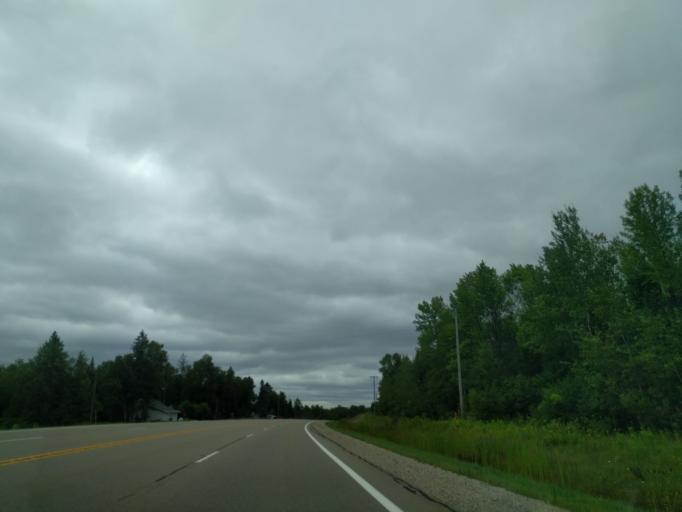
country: US
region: Michigan
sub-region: Delta County
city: Escanaba
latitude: 45.5467
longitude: -87.2717
